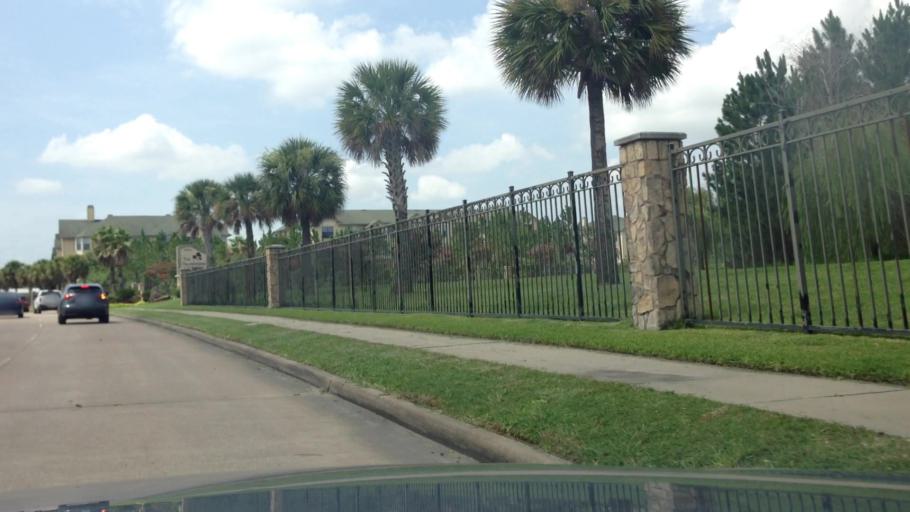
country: US
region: Texas
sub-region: Harris County
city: Jersey Village
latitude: 29.9519
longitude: -95.5473
